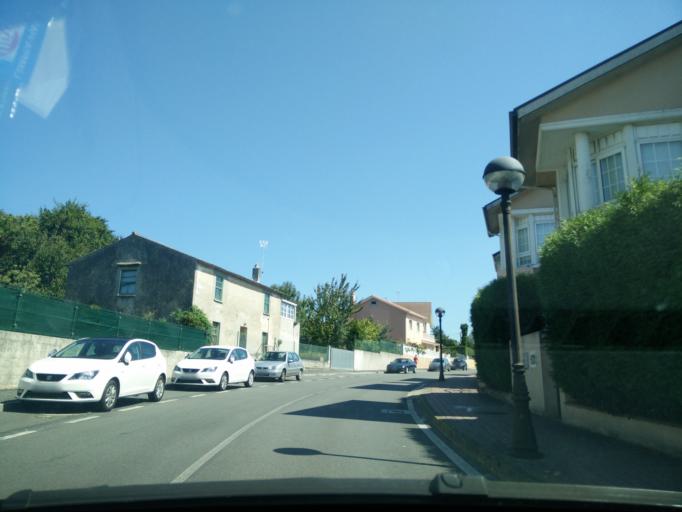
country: ES
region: Galicia
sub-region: Provincia da Coruna
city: Oleiros
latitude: 43.3417
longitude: -8.3439
